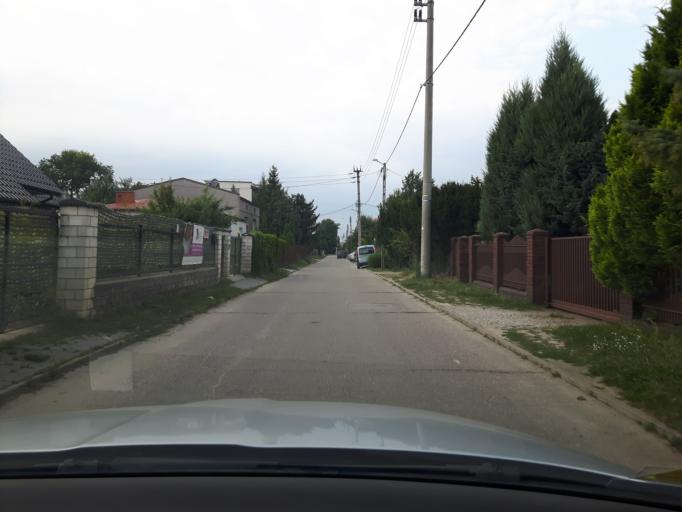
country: PL
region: Masovian Voivodeship
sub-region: Powiat wolominski
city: Zabki
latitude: 52.2818
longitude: 21.1175
